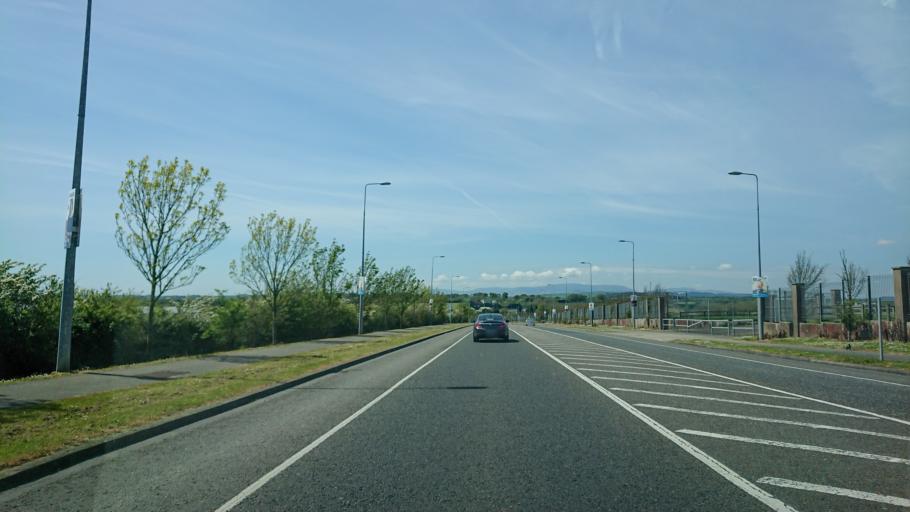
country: IE
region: Munster
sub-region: Waterford
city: Waterford
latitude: 52.2522
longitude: -7.1612
